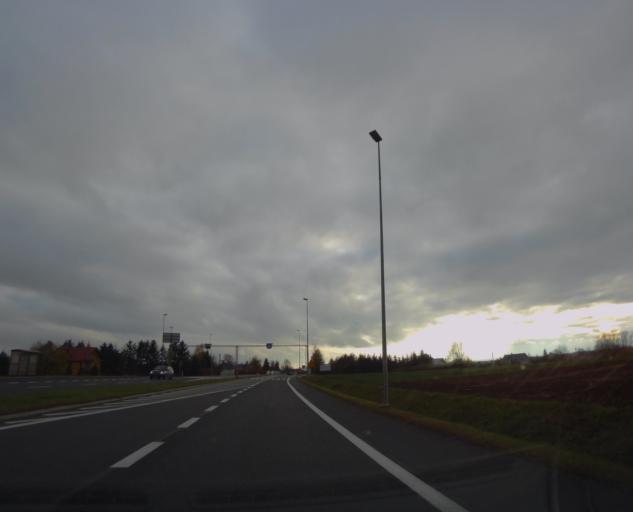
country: PL
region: Subcarpathian Voivodeship
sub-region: Powiat jaroslawski
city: Radymno
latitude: 49.9294
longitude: 22.8215
